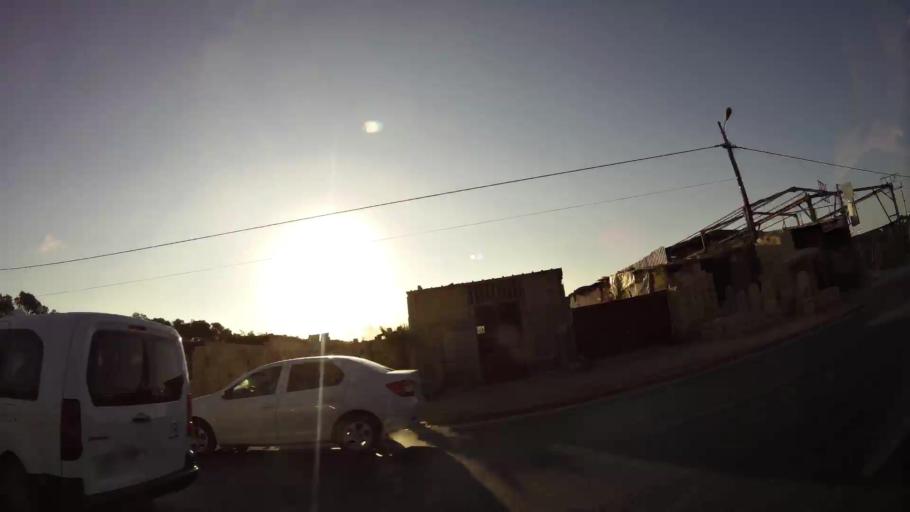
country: MA
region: Rabat-Sale-Zemmour-Zaer
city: Sale
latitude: 34.0984
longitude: -6.7607
